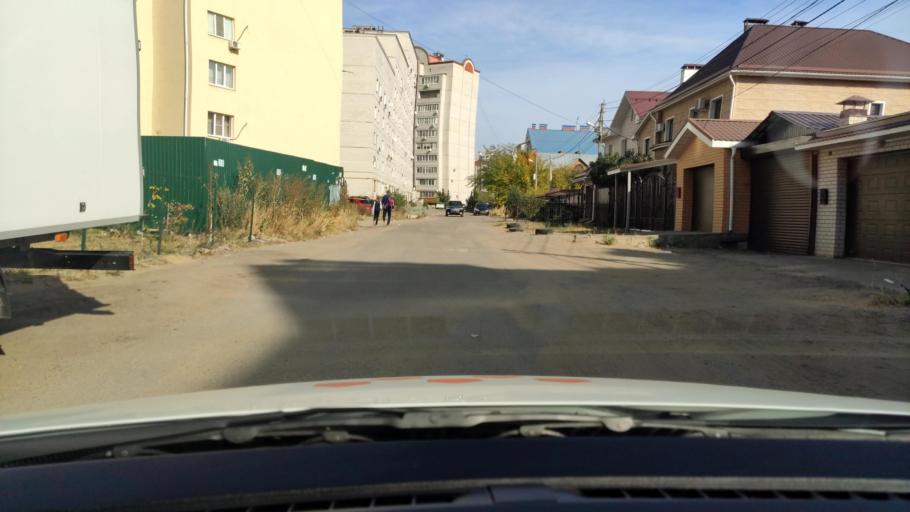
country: RU
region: Voronezj
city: Podgornoye
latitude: 51.7225
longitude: 39.1579
